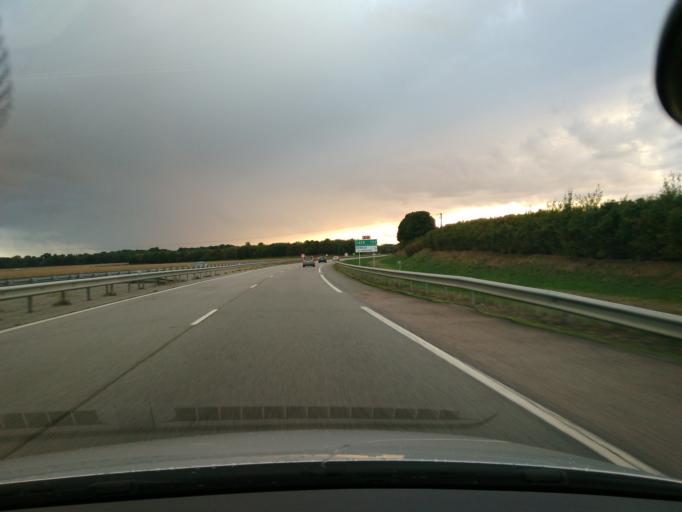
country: FR
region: Haute-Normandie
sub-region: Departement de l'Eure
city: Evreux
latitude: 49.0007
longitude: 1.1836
